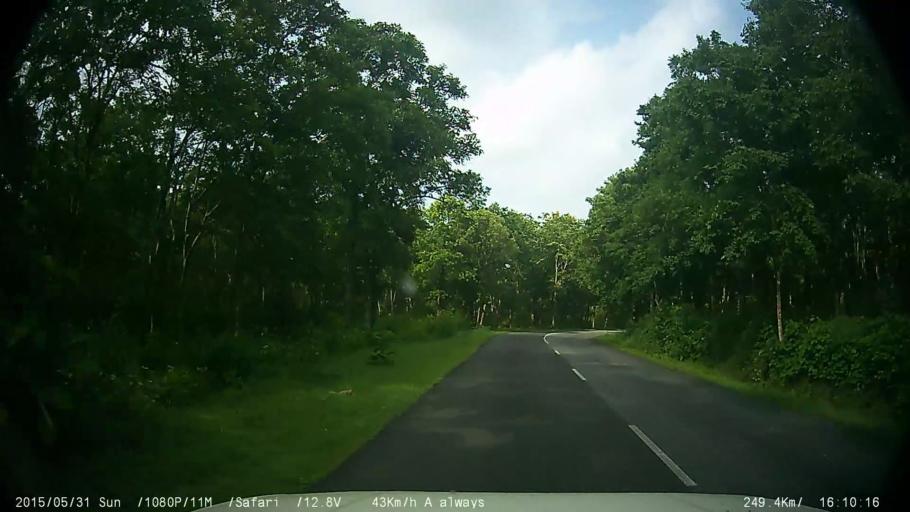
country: IN
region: Karnataka
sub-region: Mysore
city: Sargur
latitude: 11.7302
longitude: 76.4374
